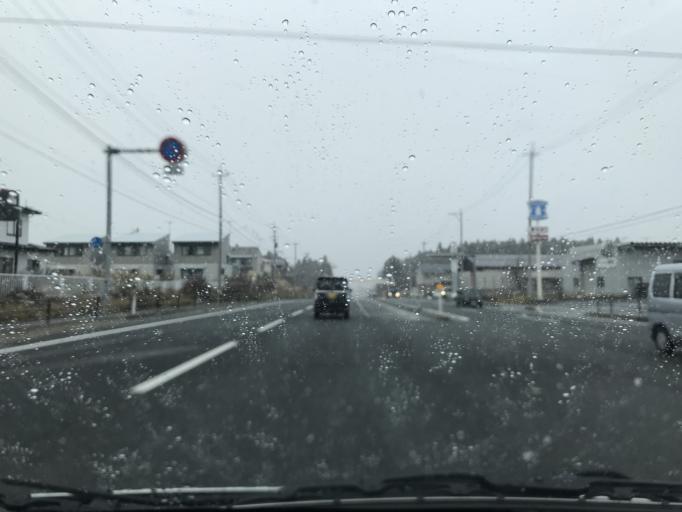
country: JP
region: Iwate
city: Kitakami
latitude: 39.2635
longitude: 141.0991
